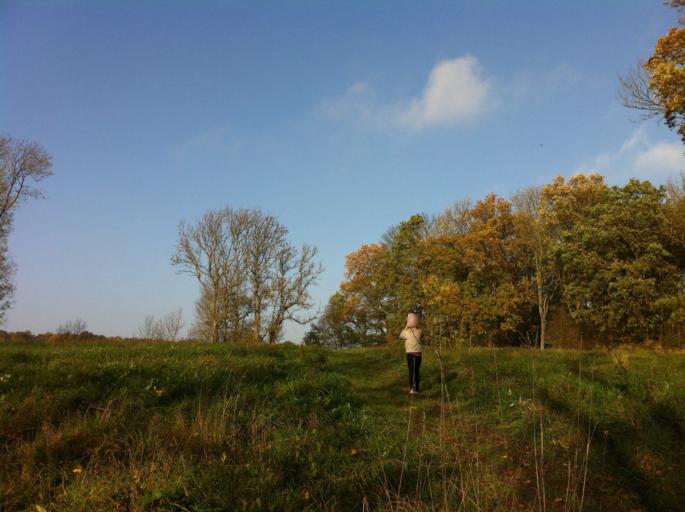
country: SE
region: Skane
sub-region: Helsingborg
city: Gantofta
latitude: 56.0000
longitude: 12.7848
